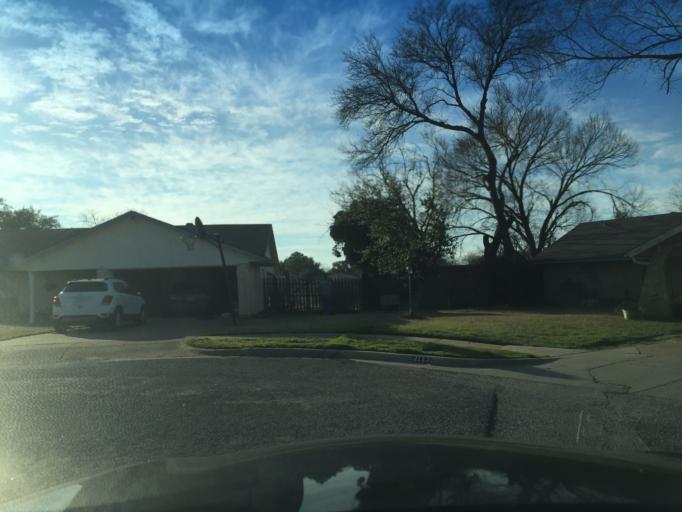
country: US
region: Texas
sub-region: Dallas County
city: Carrollton
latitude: 32.9924
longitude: -96.8804
